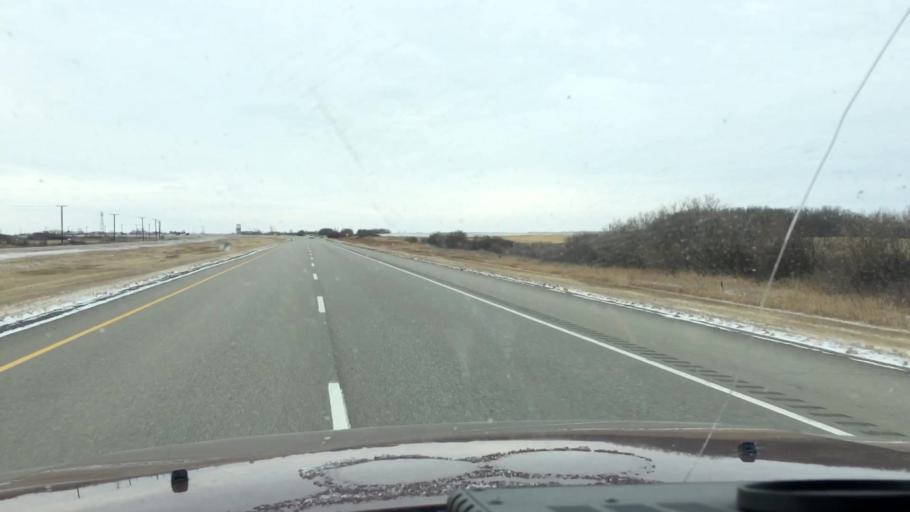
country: CA
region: Saskatchewan
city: Watrous
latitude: 51.3847
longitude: -106.1627
